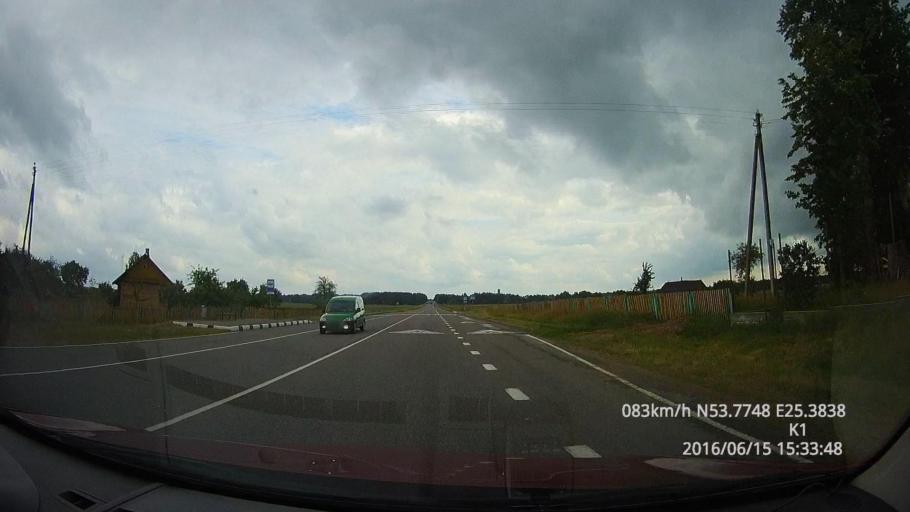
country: BY
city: Berezovka
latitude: 53.7742
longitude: 25.3842
